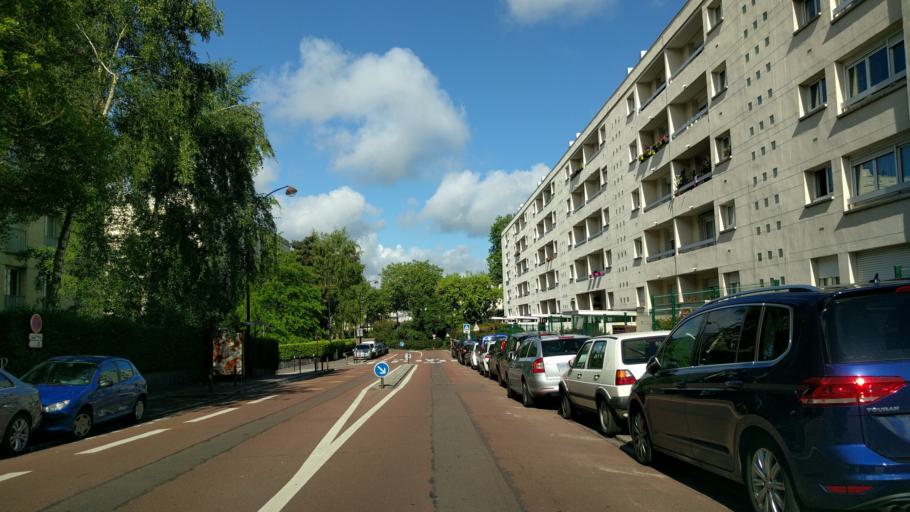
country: FR
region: Ile-de-France
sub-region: Departement des Yvelines
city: Viroflay
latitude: 48.8090
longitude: 2.1500
